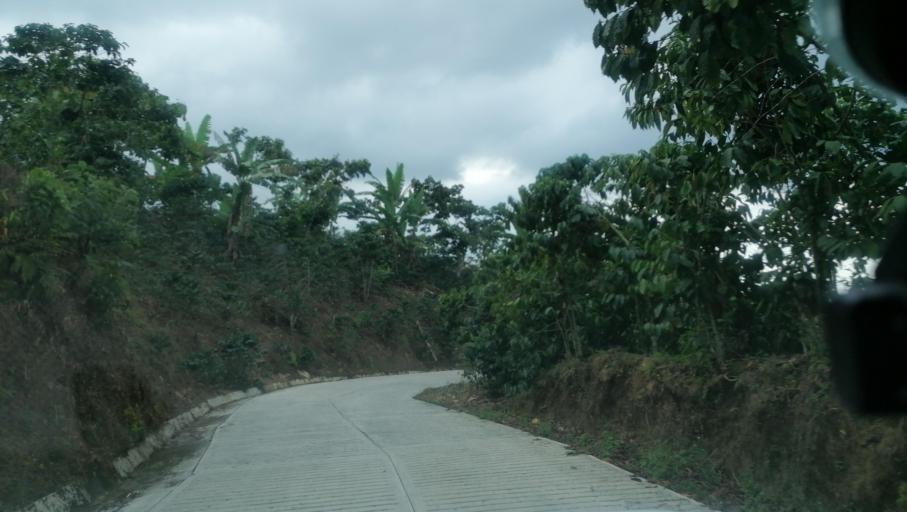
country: MX
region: Chiapas
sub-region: Cacahoatan
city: Benito Juarez
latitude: 15.0766
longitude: -92.1620
